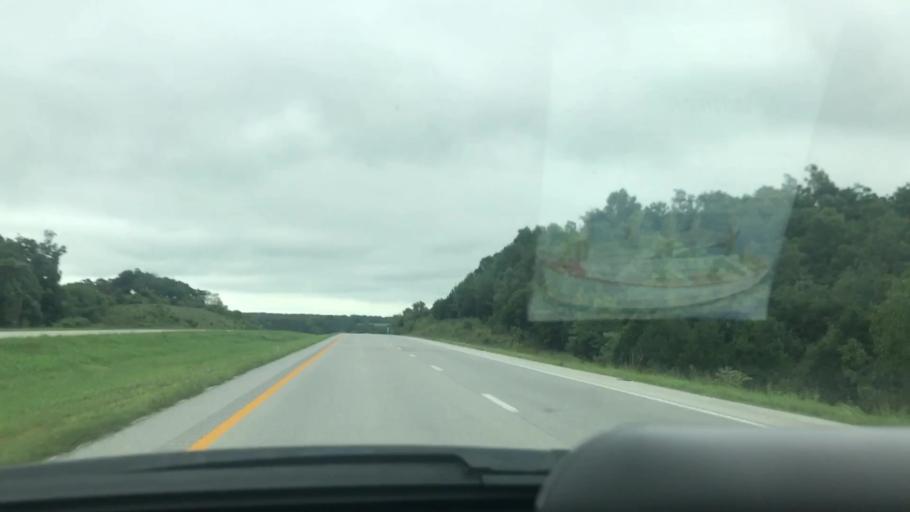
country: US
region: Missouri
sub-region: Greene County
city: Strafford
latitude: 37.2861
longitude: -93.1920
